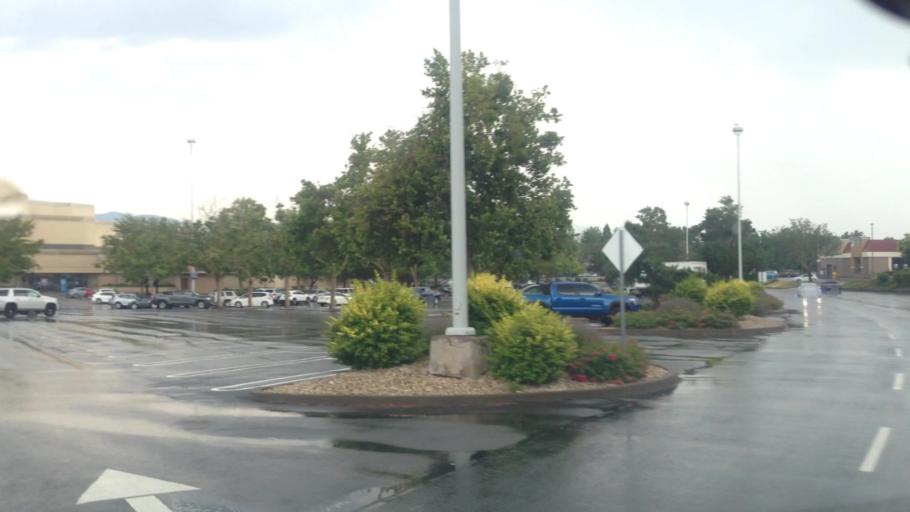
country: US
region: Nevada
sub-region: Washoe County
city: Reno
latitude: 39.4738
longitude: -119.7863
